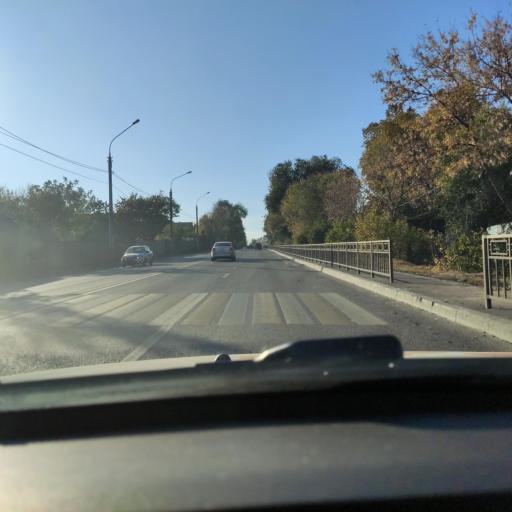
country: RU
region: Voronezj
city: Voronezh
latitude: 51.6341
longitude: 39.2015
